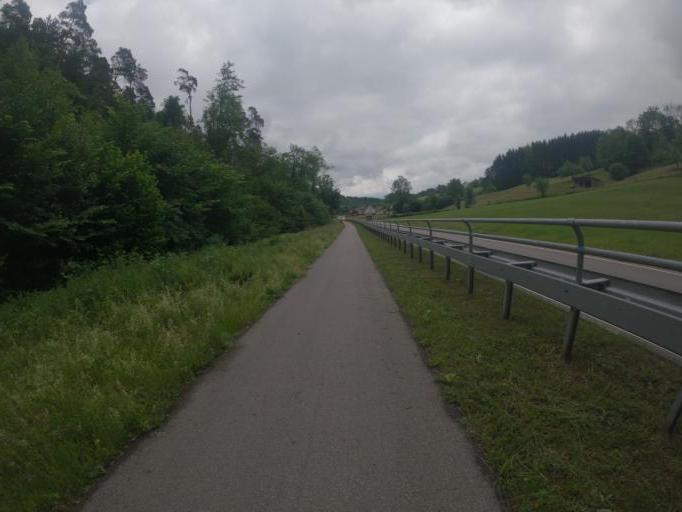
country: DE
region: Baden-Wuerttemberg
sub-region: Regierungsbezirk Stuttgart
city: Ebersbach an der Fils
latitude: 48.7303
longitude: 9.5560
